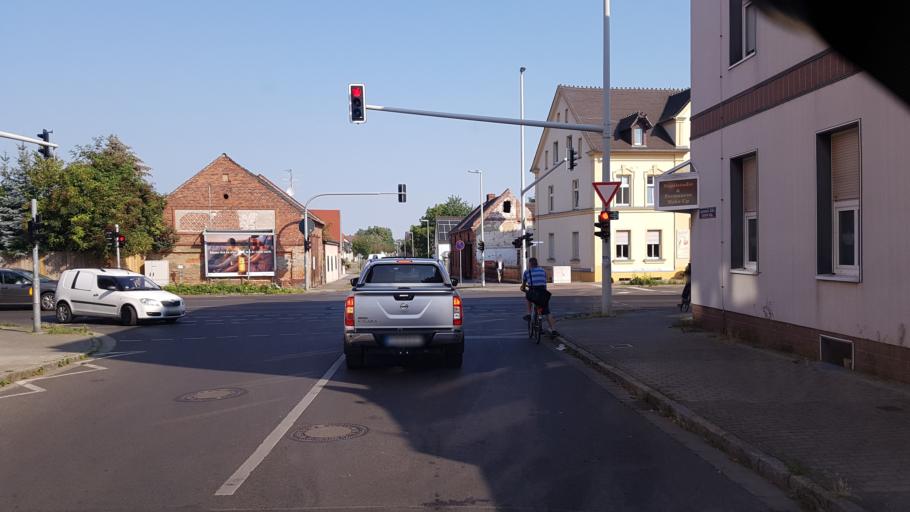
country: DE
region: Brandenburg
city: Cottbus
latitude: 51.7541
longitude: 14.3032
